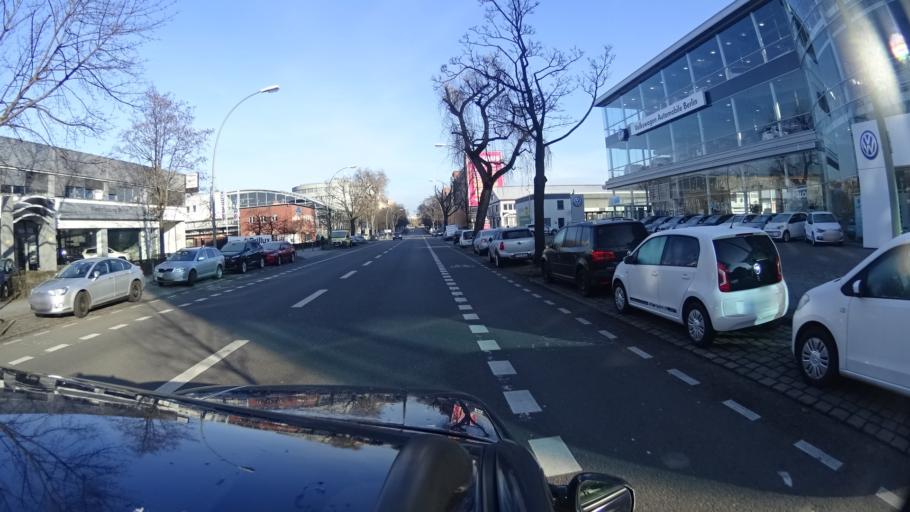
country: DE
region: Berlin
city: Moabit
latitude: 52.5189
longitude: 13.3262
